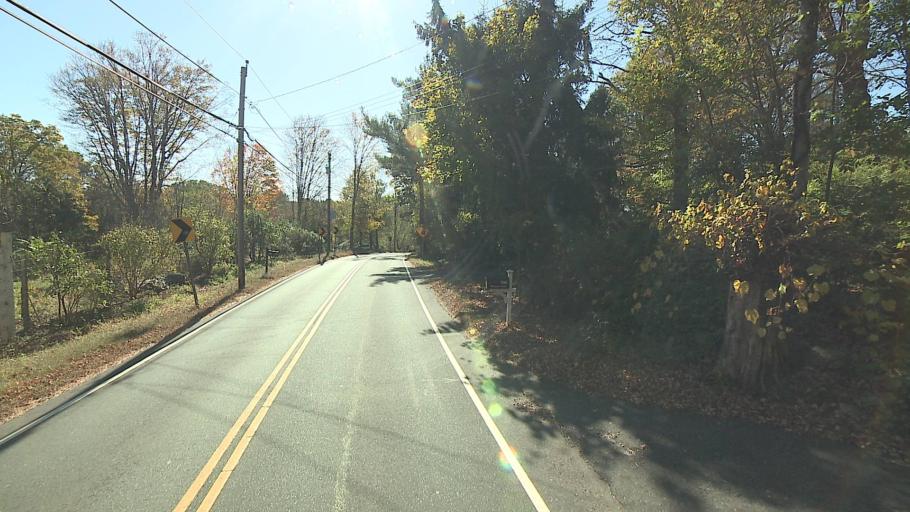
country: US
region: Connecticut
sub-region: Fairfield County
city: Trumbull
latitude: 41.2512
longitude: -73.3025
